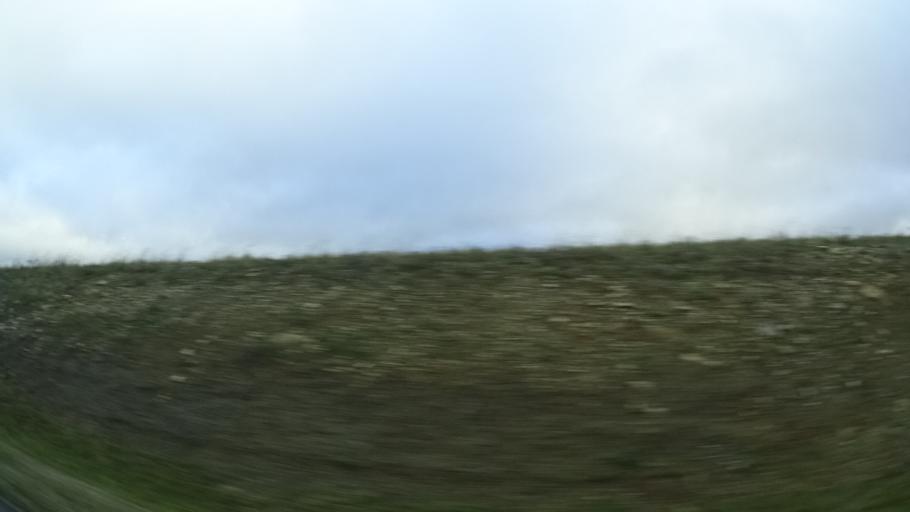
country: DE
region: Thuringia
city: Stadtilm
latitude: 50.7396
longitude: 11.0783
